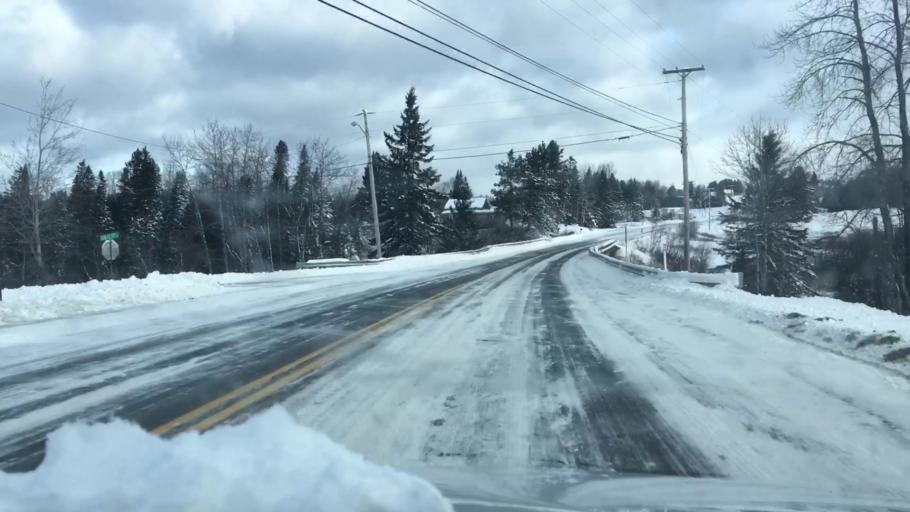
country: US
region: Maine
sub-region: Aroostook County
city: Caribou
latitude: 46.9775
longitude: -68.0356
